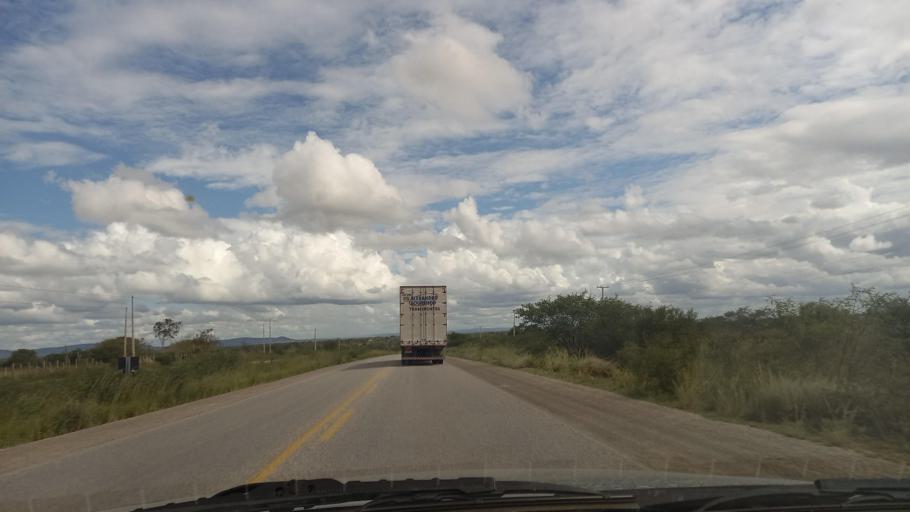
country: BR
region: Pernambuco
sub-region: Cachoeirinha
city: Cachoeirinha
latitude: -8.4036
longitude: -36.1852
